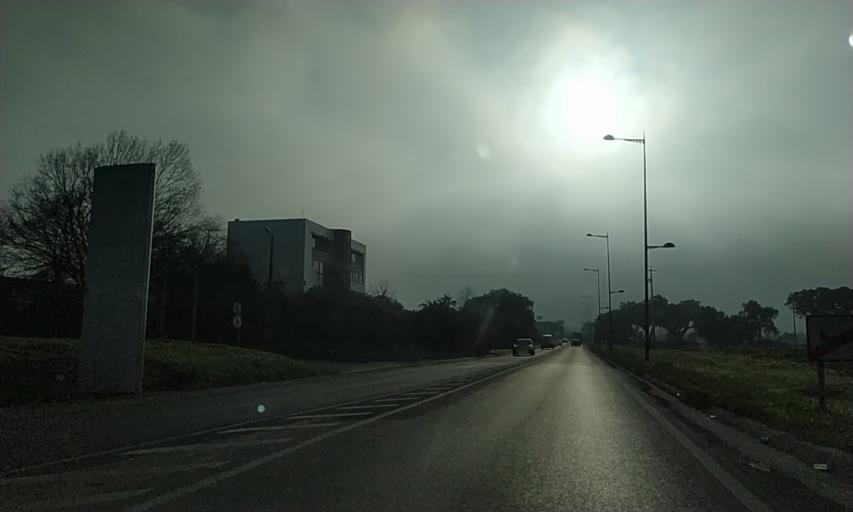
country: PT
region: Setubal
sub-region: Montijo
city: Montijo
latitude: 38.6929
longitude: -8.9504
